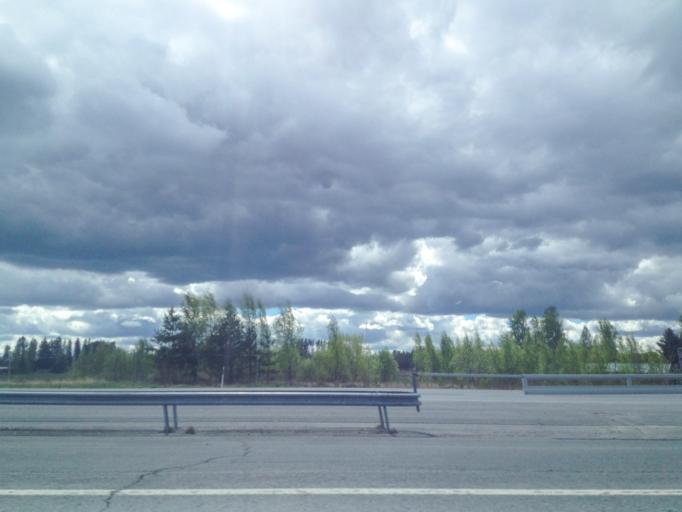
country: FI
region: Pirkanmaa
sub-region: Etelae-Pirkanmaa
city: Akaa
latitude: 61.1661
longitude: 23.9484
